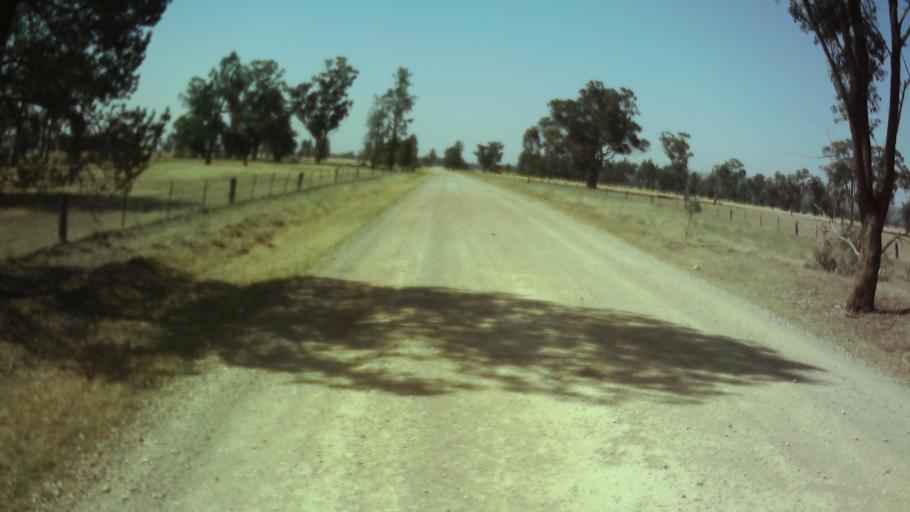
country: AU
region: New South Wales
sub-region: Weddin
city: Grenfell
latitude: -34.0209
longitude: 147.9144
